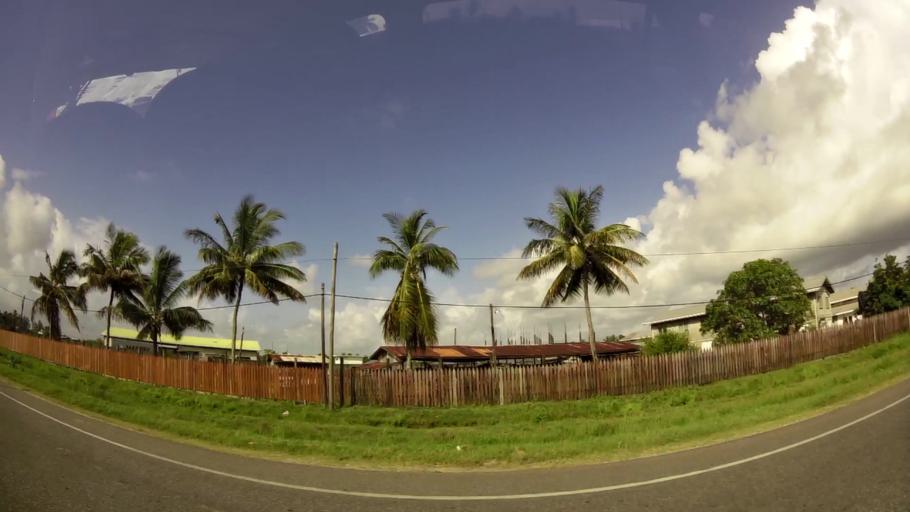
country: GY
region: Demerara-Mahaica
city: Mahaica Village
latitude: 6.7621
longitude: -57.9877
